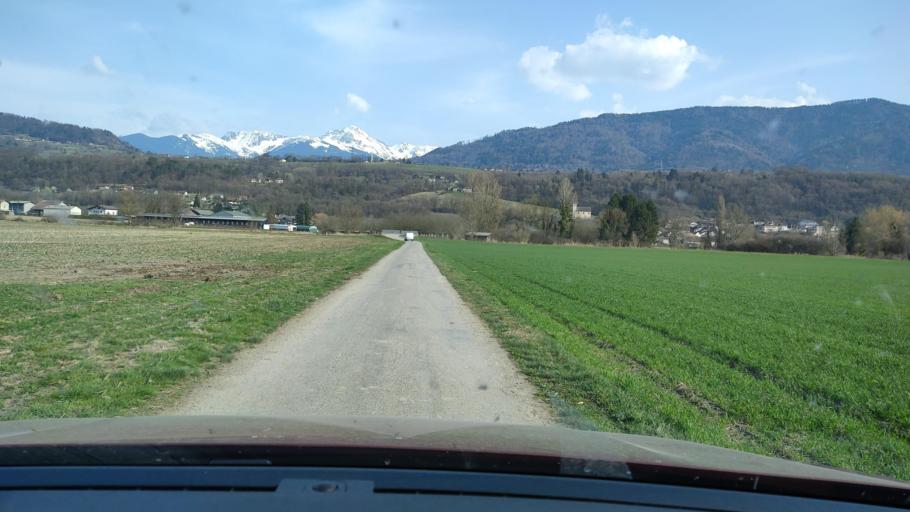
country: FR
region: Rhone-Alpes
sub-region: Departement de l'Isere
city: Pontcharra
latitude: 45.4531
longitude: 6.0320
